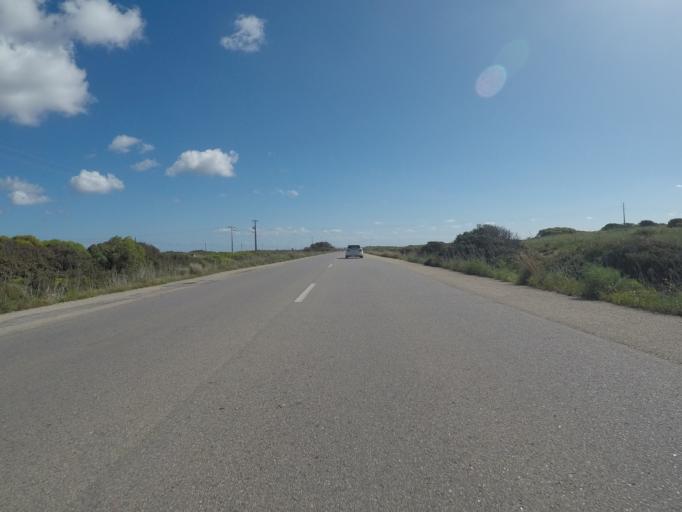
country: PT
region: Faro
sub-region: Vila do Bispo
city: Sagres
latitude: 37.0449
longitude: -8.9303
